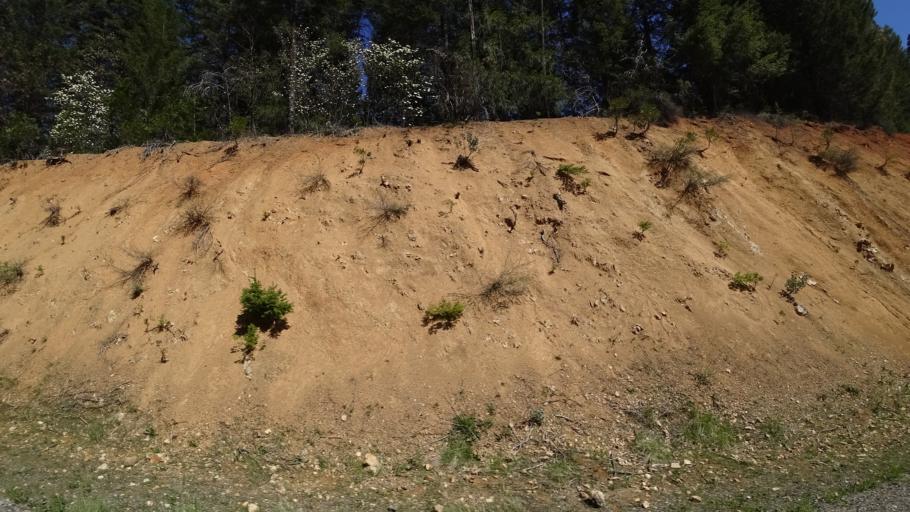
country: US
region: California
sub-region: Trinity County
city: Lewiston
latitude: 40.8957
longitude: -122.7918
